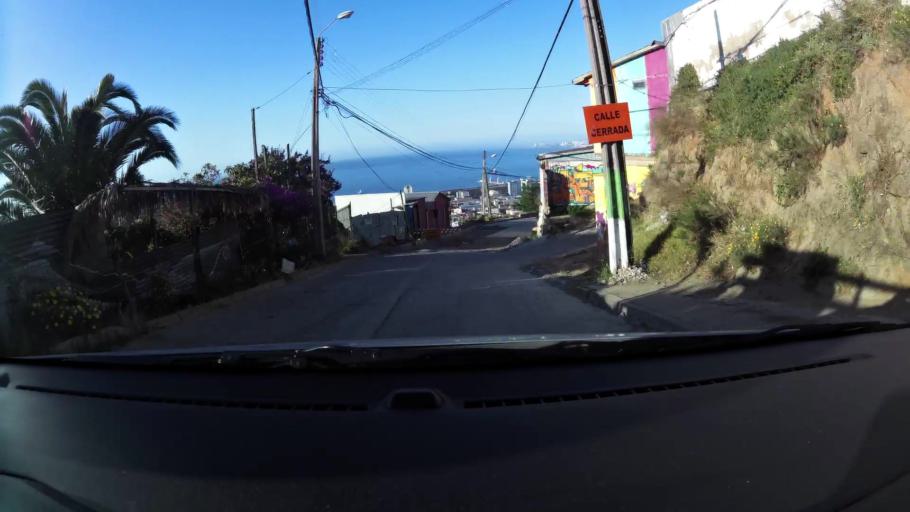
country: CL
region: Valparaiso
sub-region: Provincia de Valparaiso
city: Valparaiso
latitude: -33.0562
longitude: -71.6145
